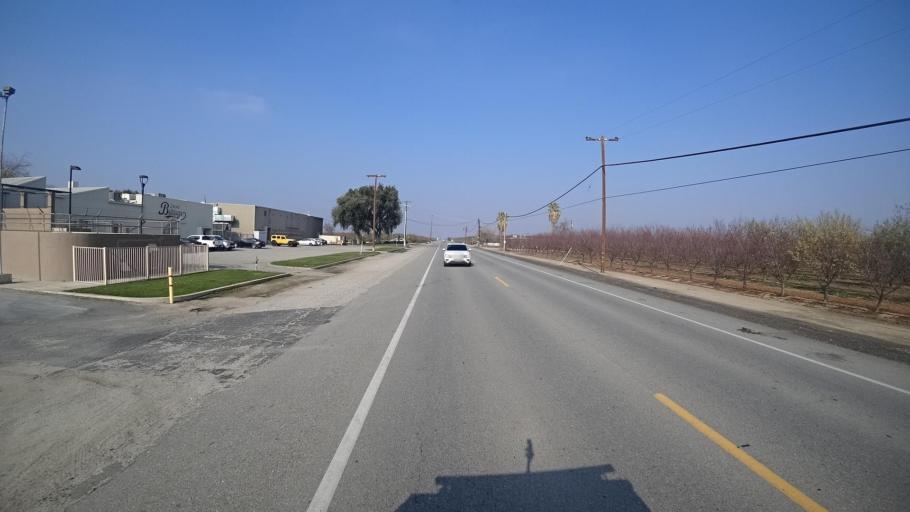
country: US
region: California
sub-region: Kern County
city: Greenfield
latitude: 35.2220
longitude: -119.1100
